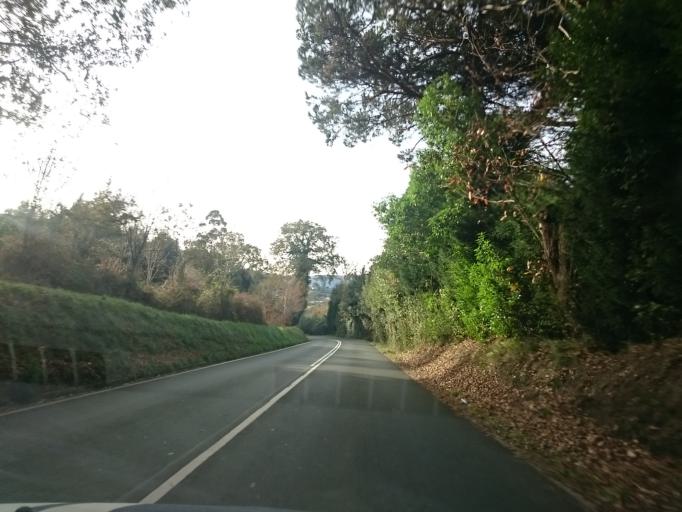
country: ES
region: Asturias
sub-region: Province of Asturias
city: Gijon
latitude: 43.5137
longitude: -5.6149
